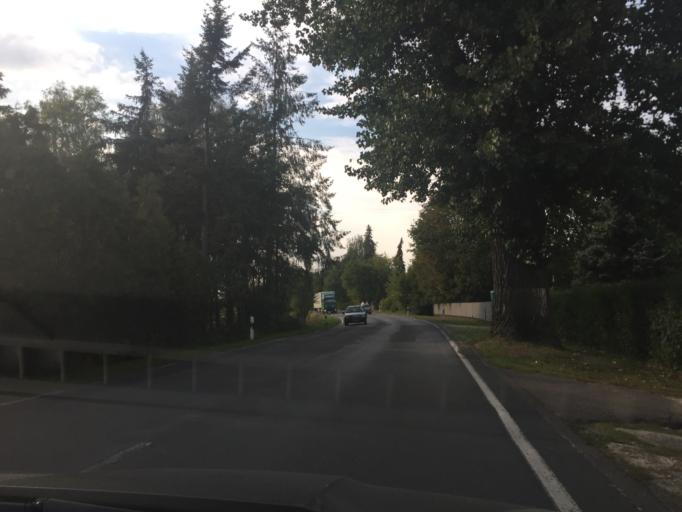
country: DE
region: Brandenburg
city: Spreenhagen
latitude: 52.3537
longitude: 13.8568
